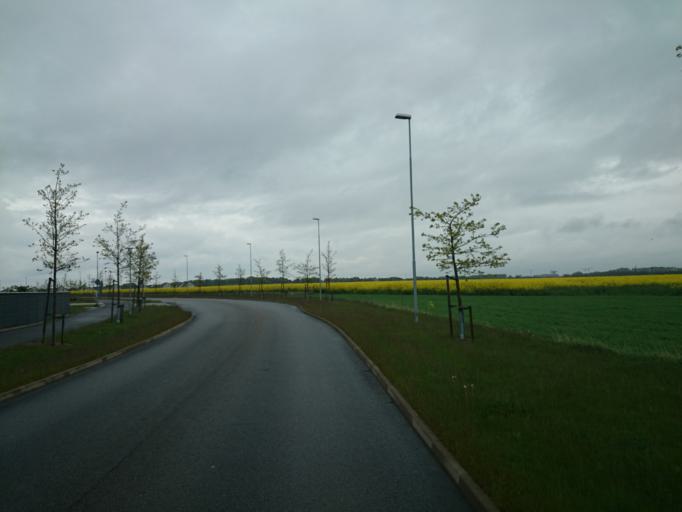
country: SE
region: Skane
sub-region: Malmo
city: Bunkeflostrand
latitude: 55.5452
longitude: 12.9285
